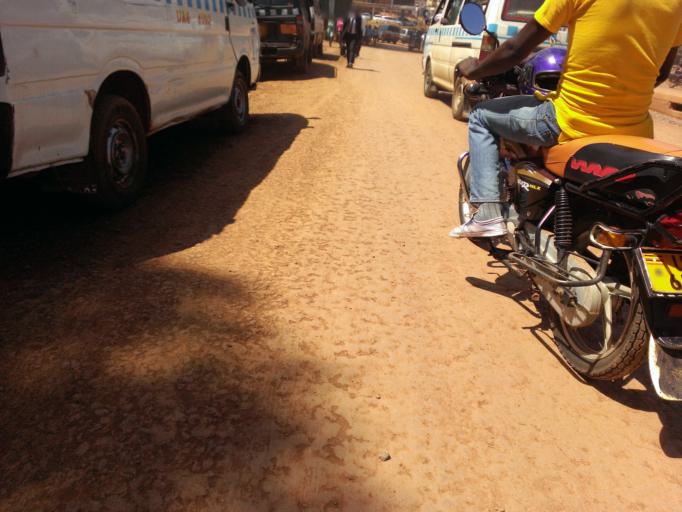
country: UG
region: Central Region
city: Kampala Central Division
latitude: 0.3292
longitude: 32.5718
